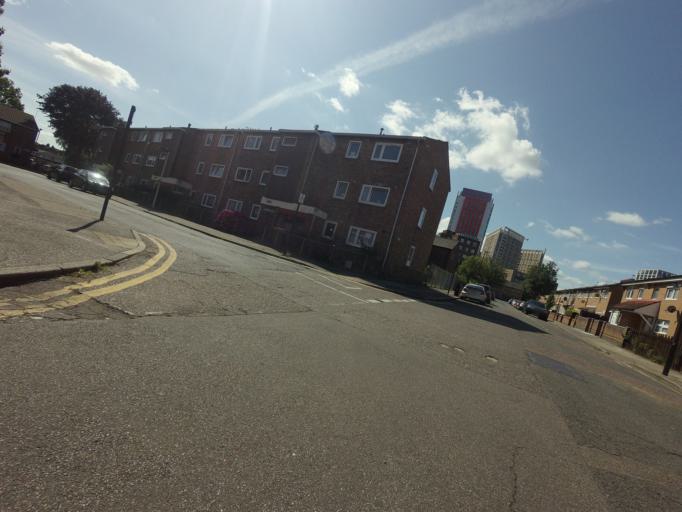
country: GB
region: England
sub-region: Greater London
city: Poplar
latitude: 51.5181
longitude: 0.0092
